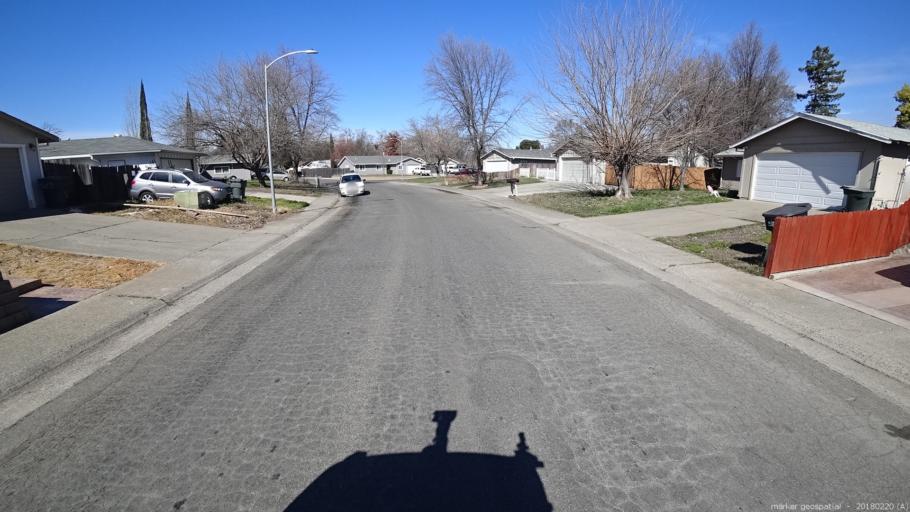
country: US
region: California
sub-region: Sacramento County
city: Orangevale
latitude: 38.7047
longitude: -121.2366
